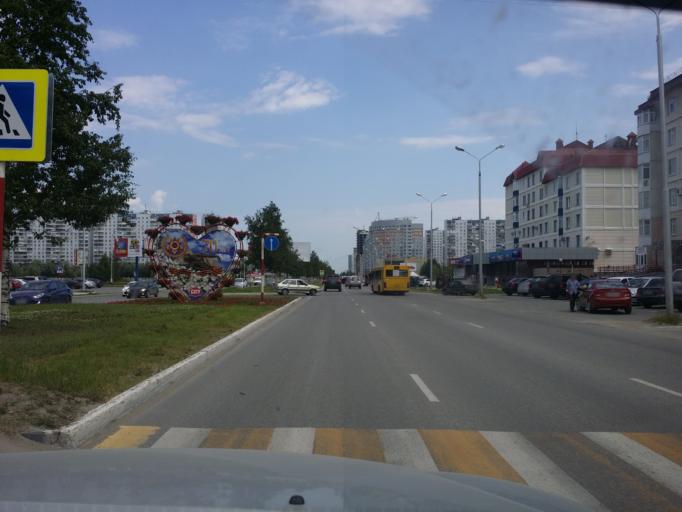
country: RU
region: Khanty-Mansiyskiy Avtonomnyy Okrug
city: Nizhnevartovsk
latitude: 60.9365
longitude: 76.5831
